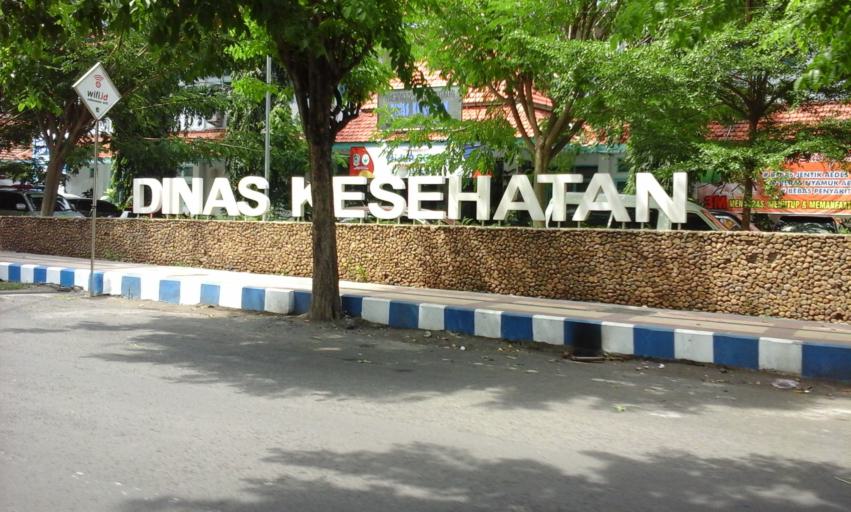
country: ID
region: East Java
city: Wirodayan
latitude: -8.2084
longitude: 114.3671
